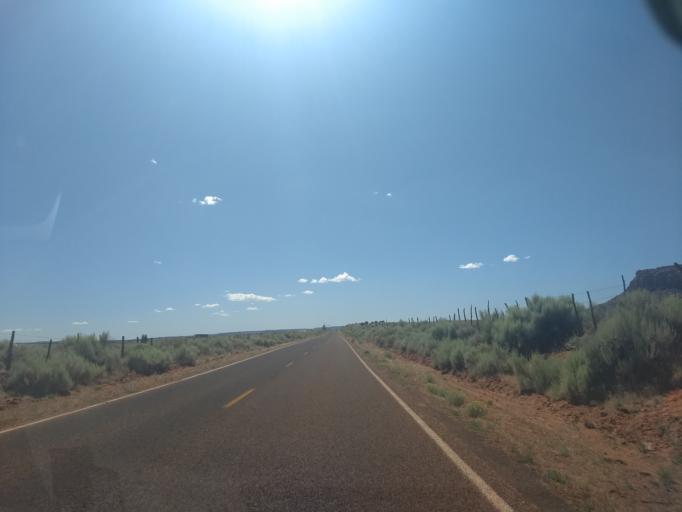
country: US
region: Arizona
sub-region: Mohave County
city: Colorado City
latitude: 36.9469
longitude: -112.9091
